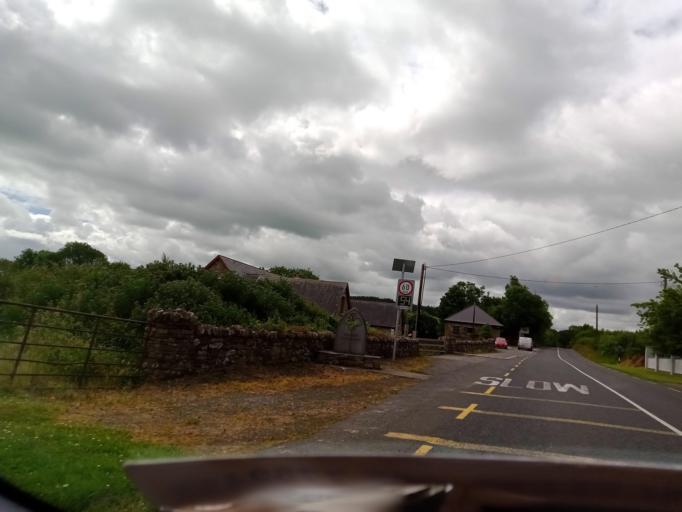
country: IE
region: Leinster
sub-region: Kilkenny
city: Thomastown
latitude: 52.4753
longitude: -7.2601
